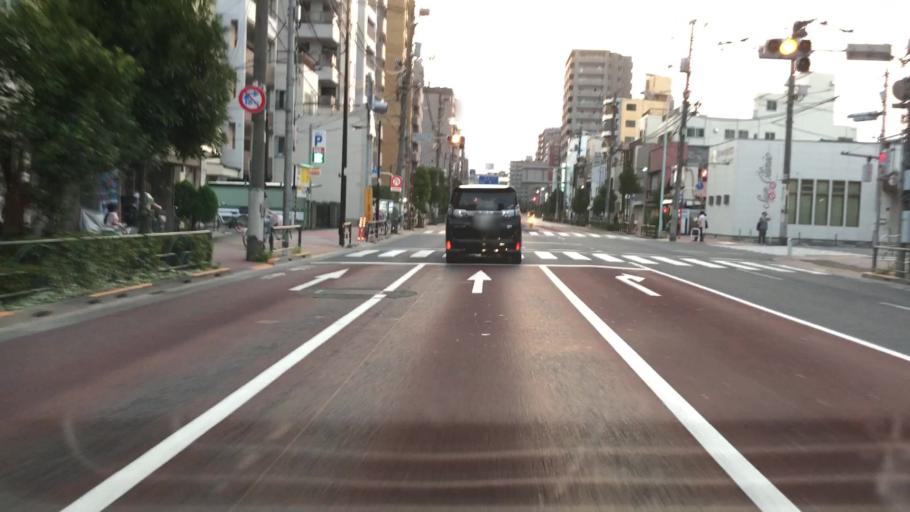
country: JP
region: Saitama
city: Soka
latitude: 35.7354
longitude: 139.7822
